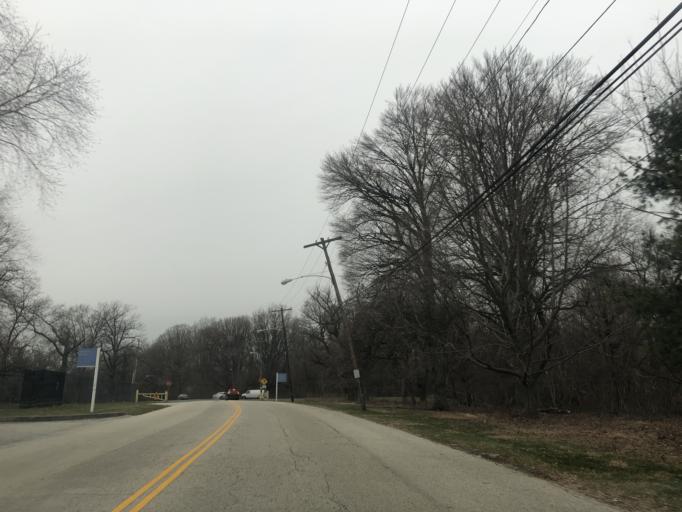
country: US
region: Pennsylvania
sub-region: Montgomery County
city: Bala-Cynwyd
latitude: 39.9926
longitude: -75.2137
